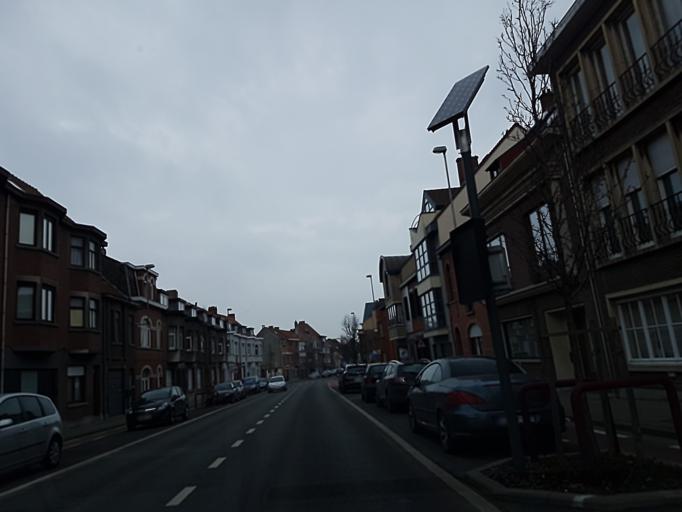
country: BE
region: Flanders
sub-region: Provincie Oost-Vlaanderen
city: Deinze
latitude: 50.9826
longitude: 3.5333
